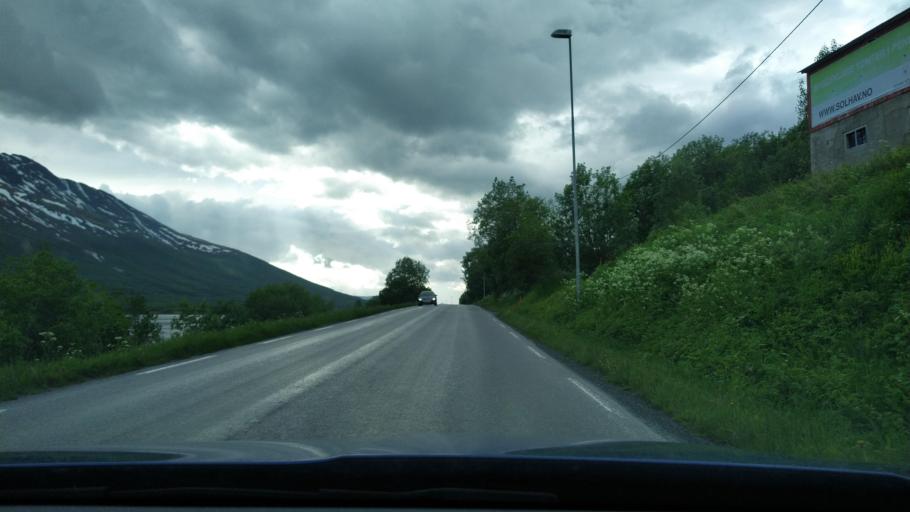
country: NO
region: Troms
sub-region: Balsfjord
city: Storsteinnes
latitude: 69.2211
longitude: 19.5286
